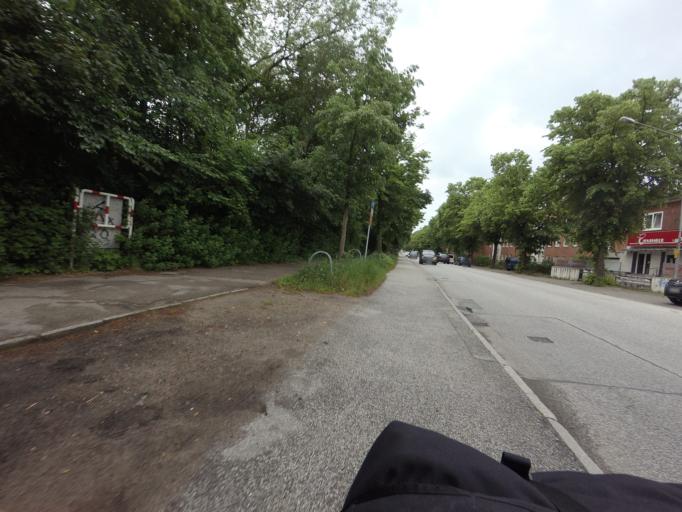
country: DE
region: Mecklenburg-Vorpommern
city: Selmsdorf
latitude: 53.9077
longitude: 10.8037
